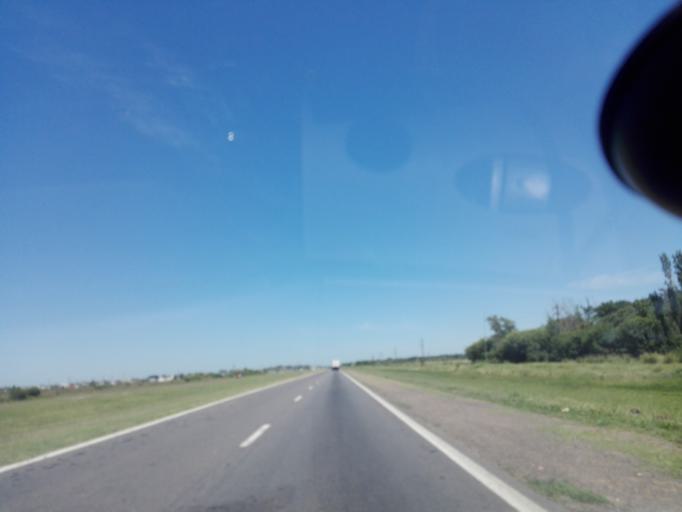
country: AR
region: Santa Fe
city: Roldan
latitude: -32.9315
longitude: -60.8659
